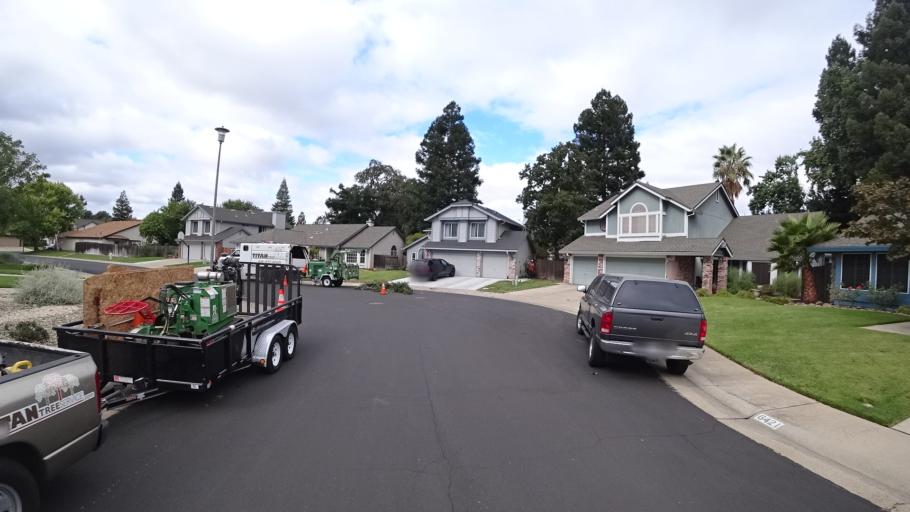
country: US
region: California
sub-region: Sacramento County
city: Laguna
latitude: 38.4148
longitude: -121.4283
